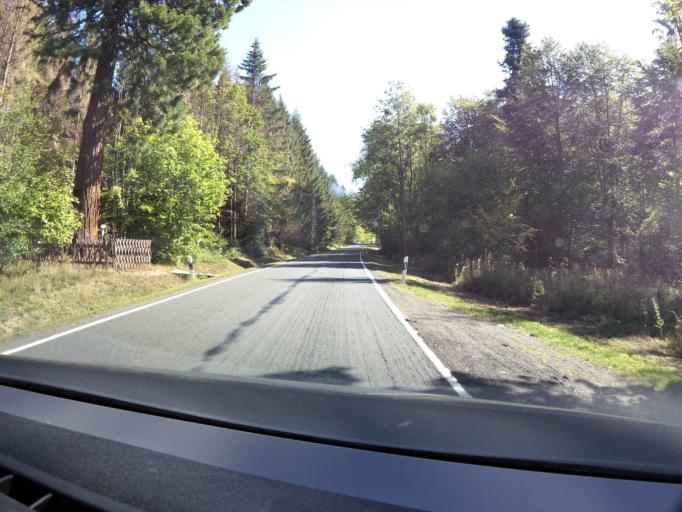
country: DE
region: Saxony-Anhalt
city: Hasselfelde
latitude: 51.6796
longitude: 10.9337
